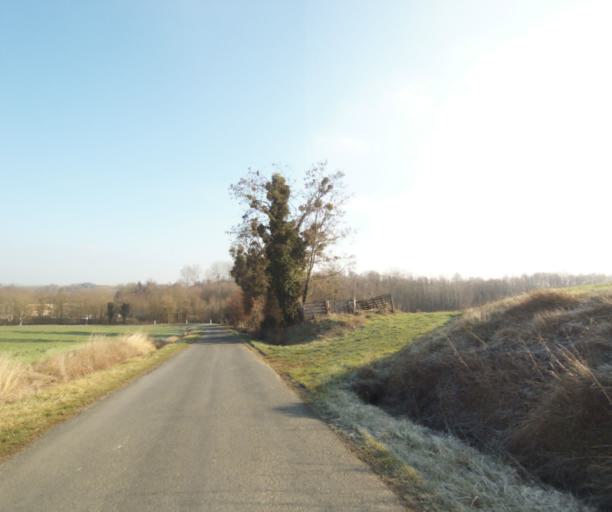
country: FR
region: Champagne-Ardenne
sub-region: Departement de la Haute-Marne
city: Wassy
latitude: 48.4704
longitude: 4.9630
